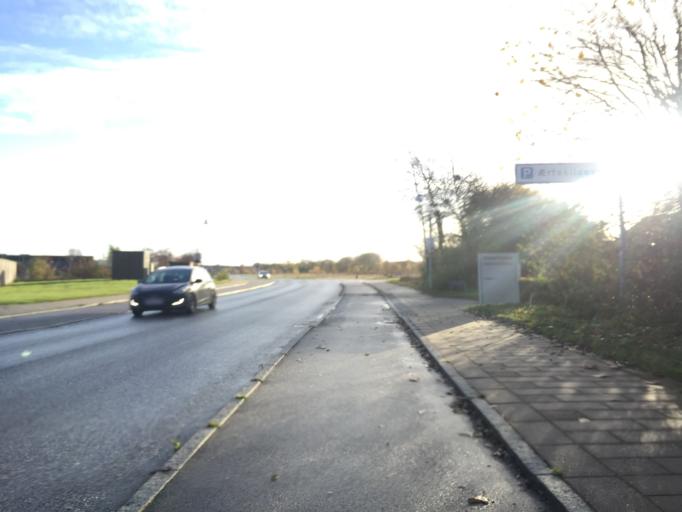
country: DK
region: Zealand
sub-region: Ringsted Kommune
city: Ringsted
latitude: 55.4516
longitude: 11.7928
